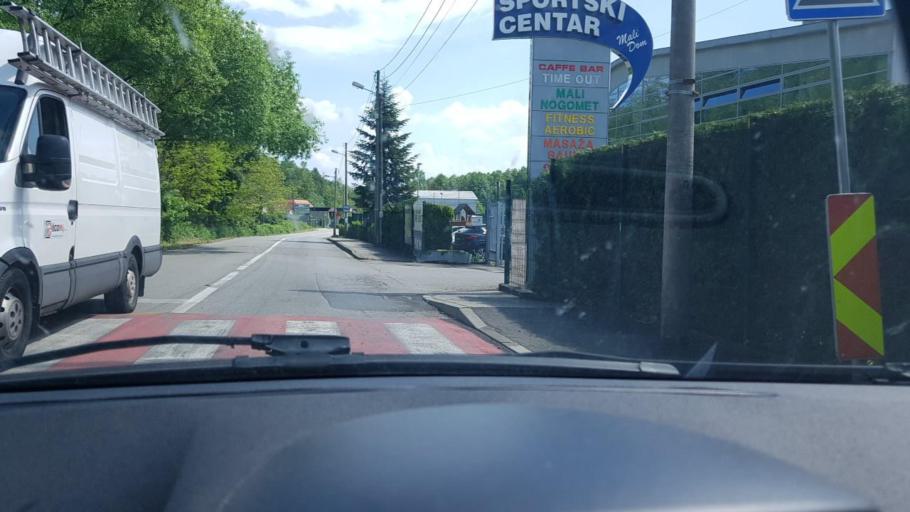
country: HR
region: Grad Zagreb
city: Dubrava
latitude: 45.8614
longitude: 16.0223
